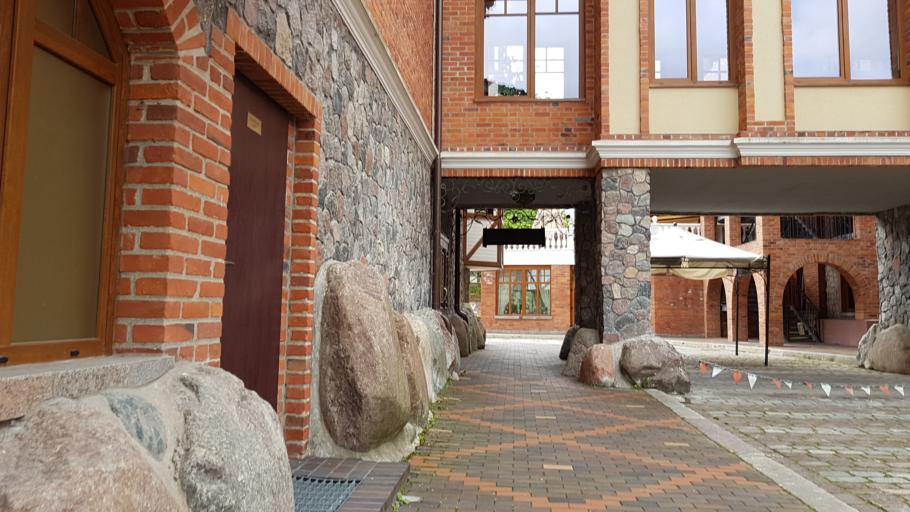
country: RU
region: Kaliningrad
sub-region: Gorod Kaliningrad
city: Kaliningrad
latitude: 54.7229
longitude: 20.5285
